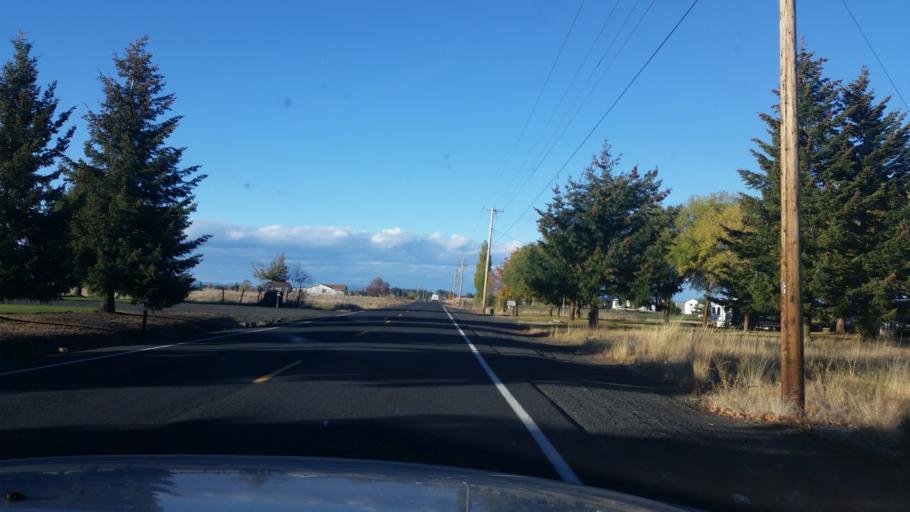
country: US
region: Washington
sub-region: Spokane County
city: Fairchild Air Force Base
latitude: 47.5904
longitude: -117.6075
